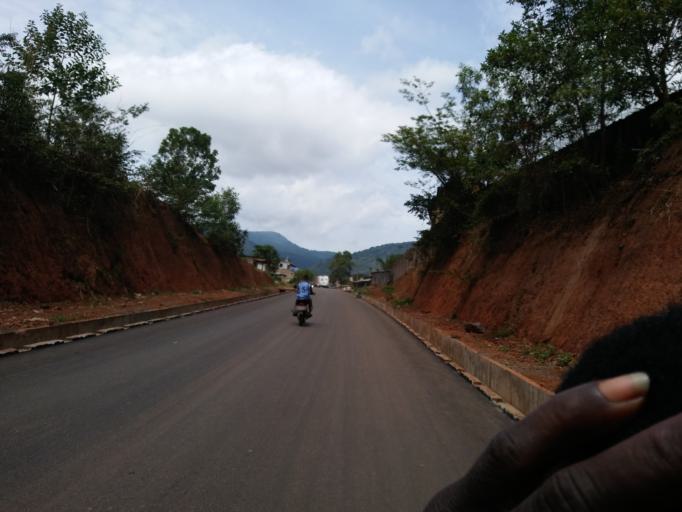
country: SL
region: Western Area
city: Hastings
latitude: 8.3981
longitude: -13.1544
